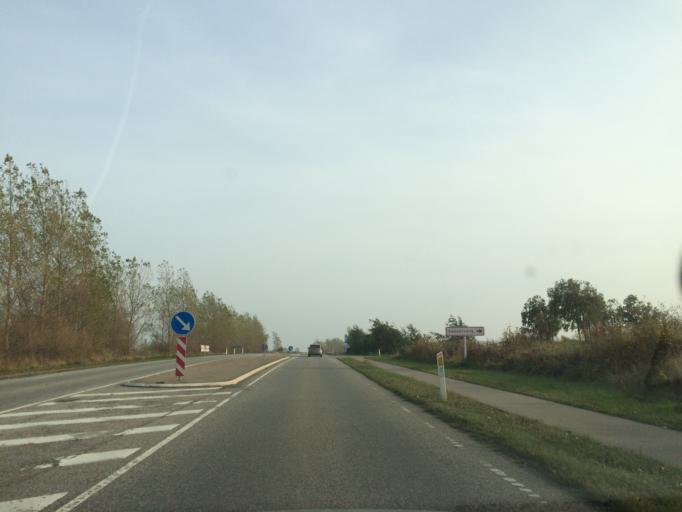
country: DK
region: Zealand
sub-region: Odsherred Kommune
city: Asnaes
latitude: 55.9745
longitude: 11.3440
